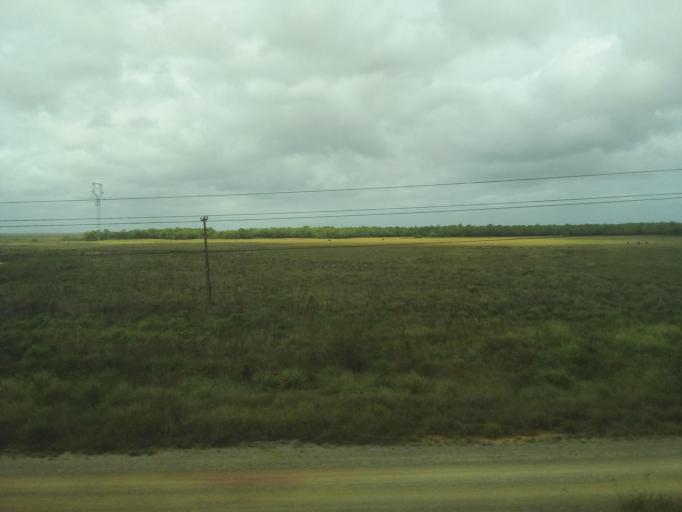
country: BR
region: Maranhao
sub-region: Icatu
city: Icatu
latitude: -2.9135
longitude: -44.3550
